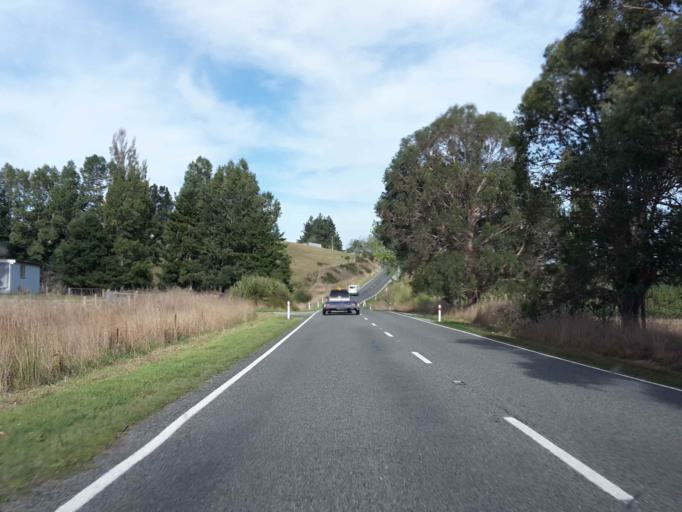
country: NZ
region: Canterbury
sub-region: Timaru District
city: Pleasant Point
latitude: -44.0938
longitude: 170.9958
